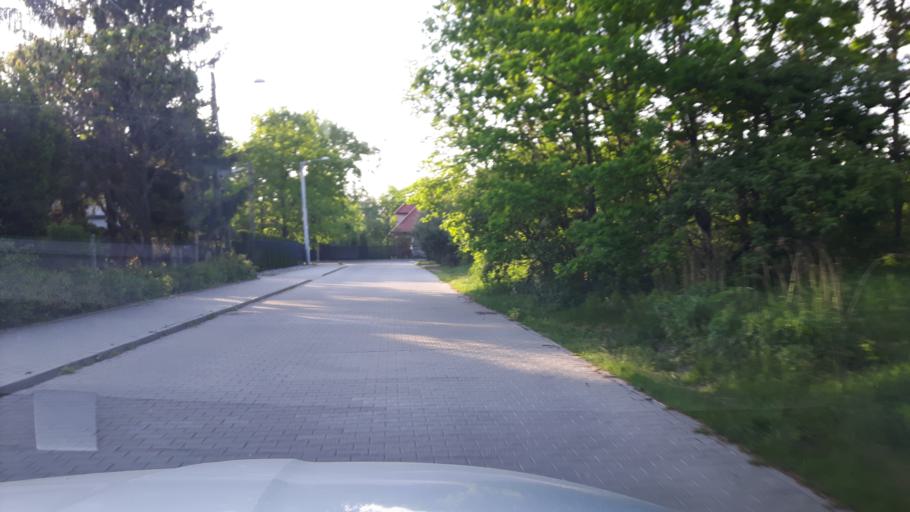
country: PL
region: Masovian Voivodeship
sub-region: Warszawa
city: Rembertow
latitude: 52.2675
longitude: 21.1498
